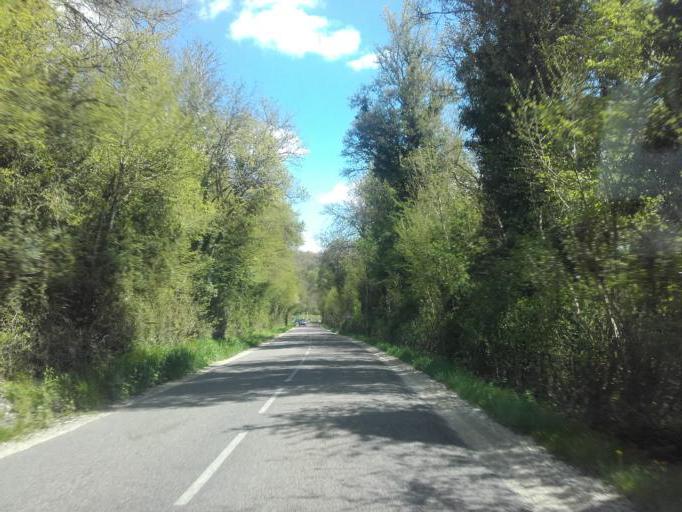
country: FR
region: Bourgogne
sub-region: Departement de la Cote-d'Or
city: Meursault
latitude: 47.0166
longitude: 4.7413
